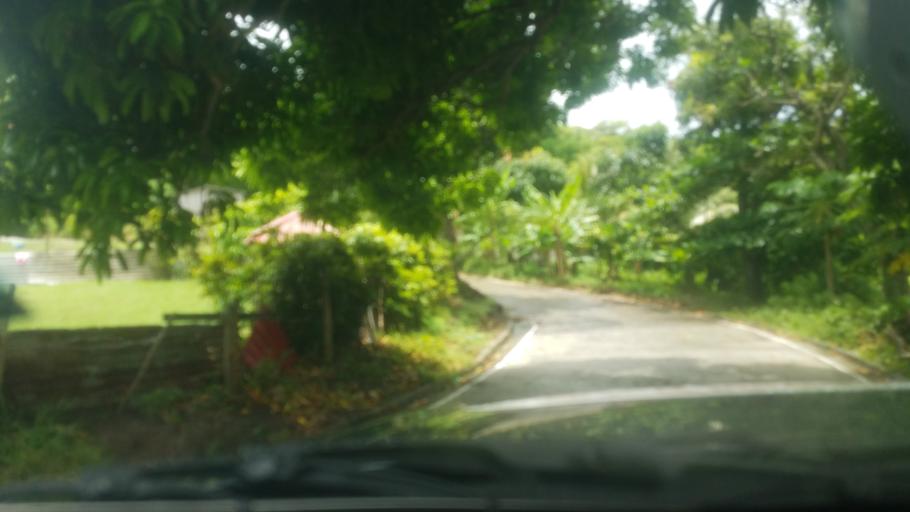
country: LC
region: Gros-Islet
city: Gros Islet
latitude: 14.0418
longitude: -60.9310
